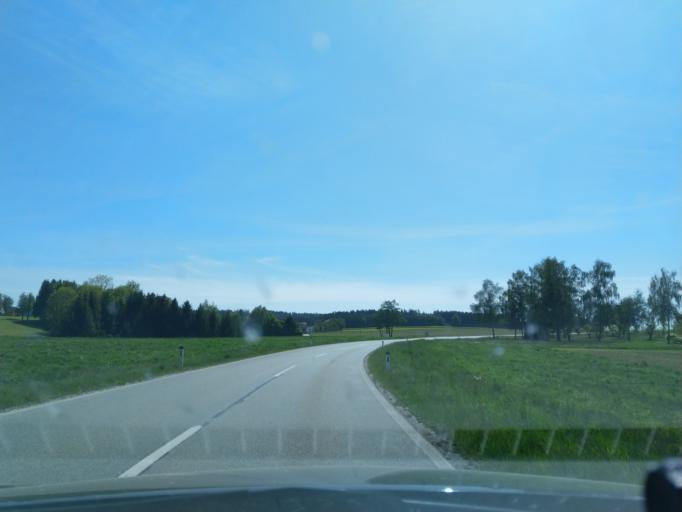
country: DE
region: Bavaria
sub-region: Lower Bavaria
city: Bad Fussing
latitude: 48.2701
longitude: 13.3529
